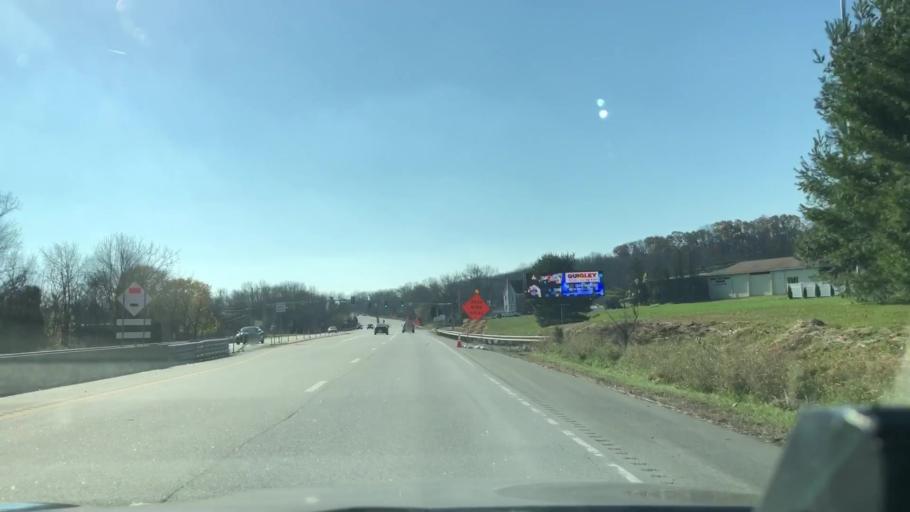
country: US
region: Pennsylvania
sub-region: Montgomery County
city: Halfway House
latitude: 40.2795
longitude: -75.6454
